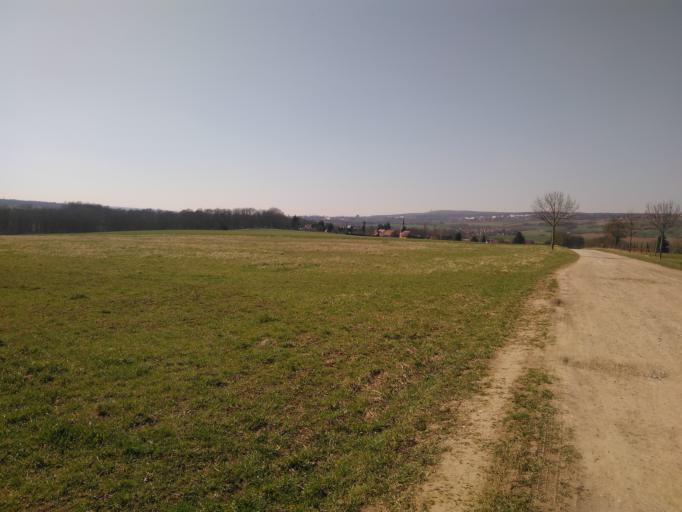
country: DE
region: Thuringia
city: Umpferstedt
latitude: 51.0010
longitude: 11.3950
